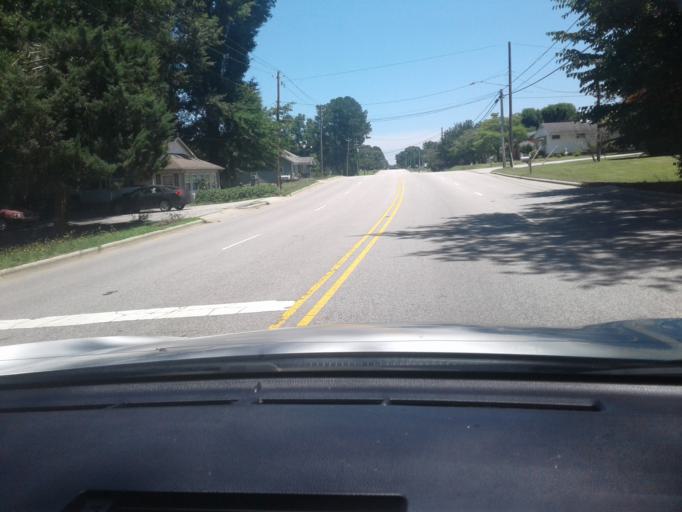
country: US
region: North Carolina
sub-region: Harnett County
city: Lillington
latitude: 35.3920
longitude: -78.8127
